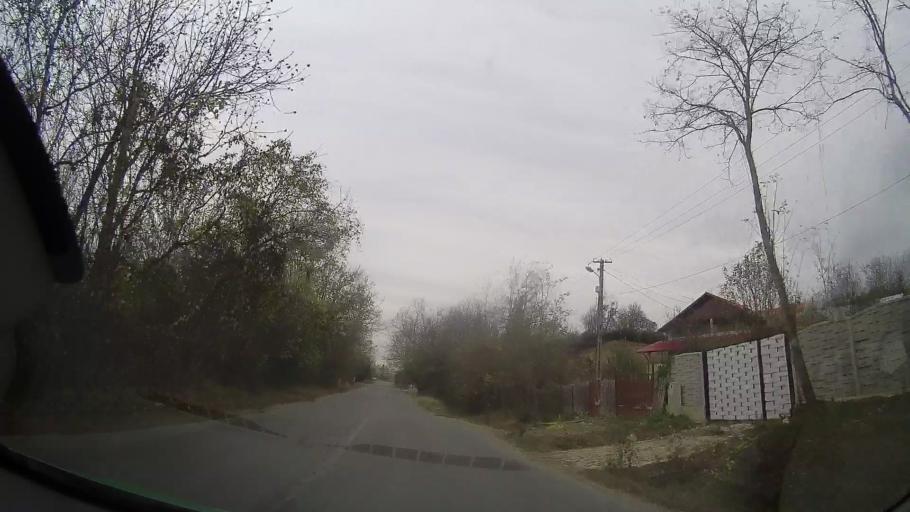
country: RO
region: Prahova
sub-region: Comuna Iordachianu
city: Iordacheanu
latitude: 45.0200
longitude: 26.2347
